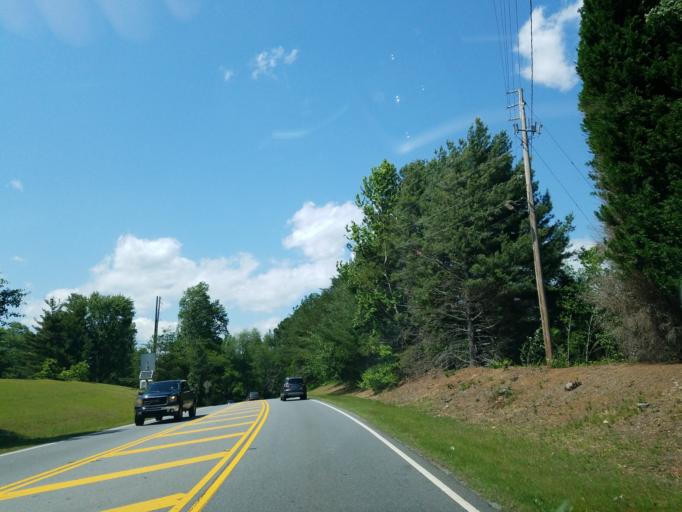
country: US
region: Georgia
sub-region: Fulton County
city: Roswell
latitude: 34.0698
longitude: -84.3509
